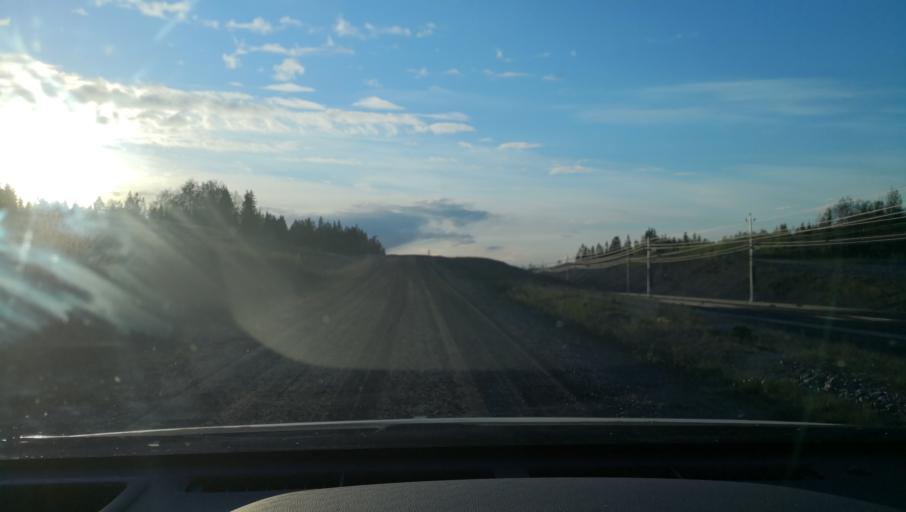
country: SE
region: OErebro
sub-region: Askersunds Kommun
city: Asbro
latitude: 58.8797
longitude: 15.1407
